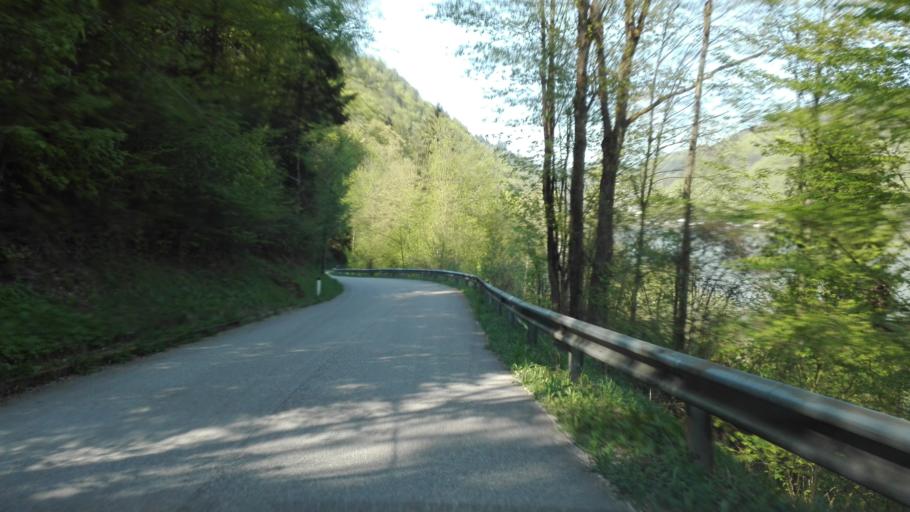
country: AT
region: Upper Austria
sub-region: Politischer Bezirk Rohrbach
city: Atzesberg
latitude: 48.4381
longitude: 13.9173
